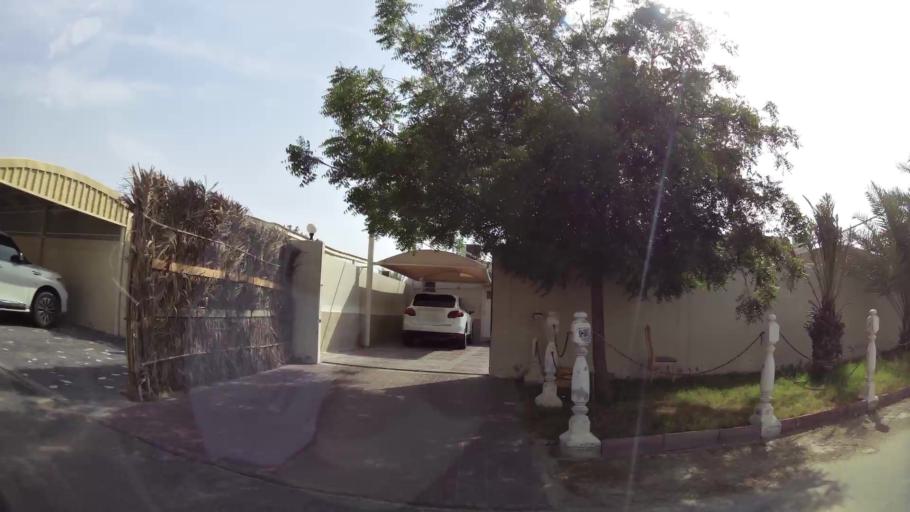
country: AE
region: Ash Shariqah
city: Sharjah
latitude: 25.2579
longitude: 55.4368
